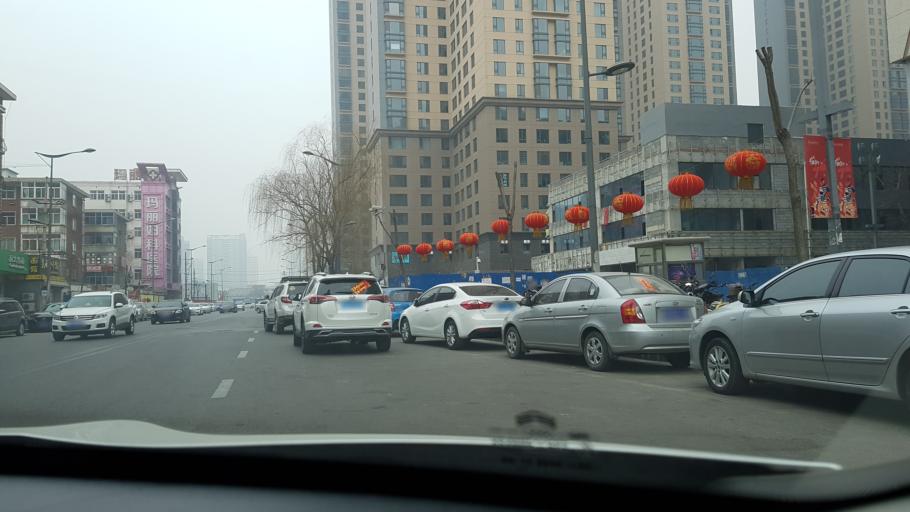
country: CN
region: Shanxi Sheng
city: Qianfeng
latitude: 37.8236
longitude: 112.5587
